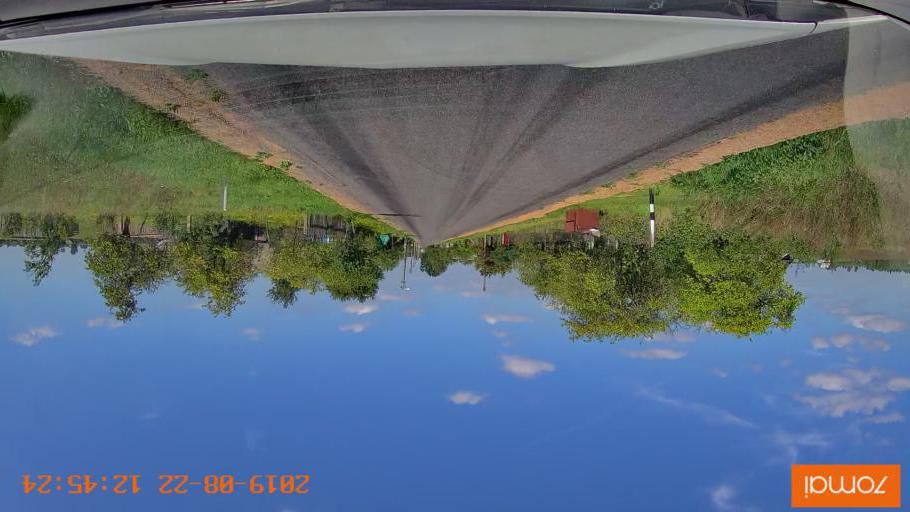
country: BY
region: Minsk
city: Prawdzinski
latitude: 53.4570
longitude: 27.6193
